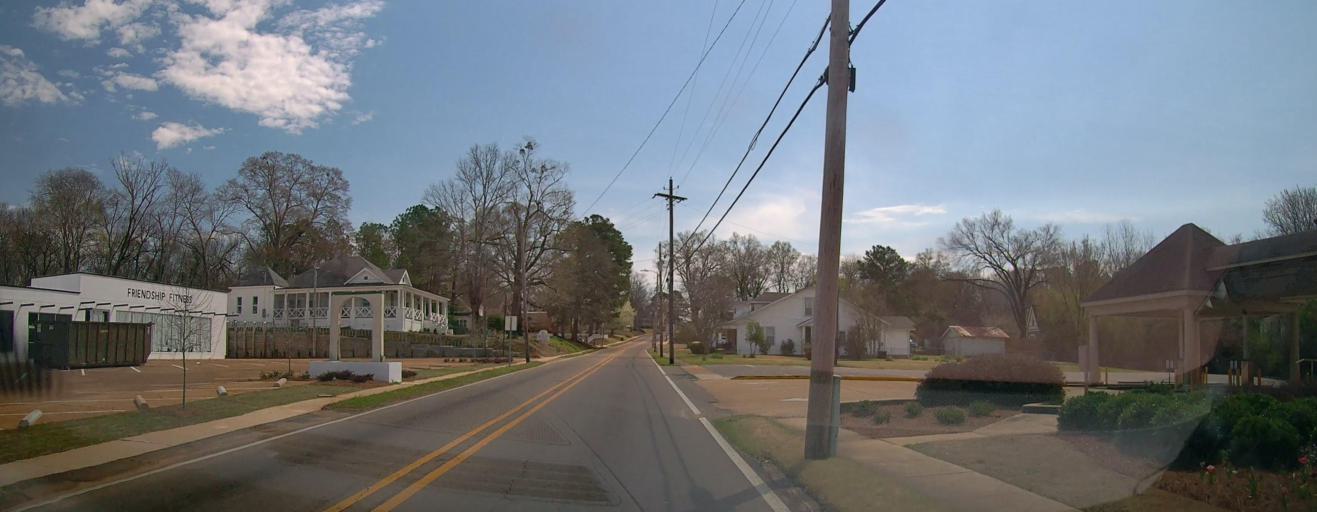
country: US
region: Mississippi
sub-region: Union County
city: New Albany
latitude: 34.4915
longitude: -89.0054
